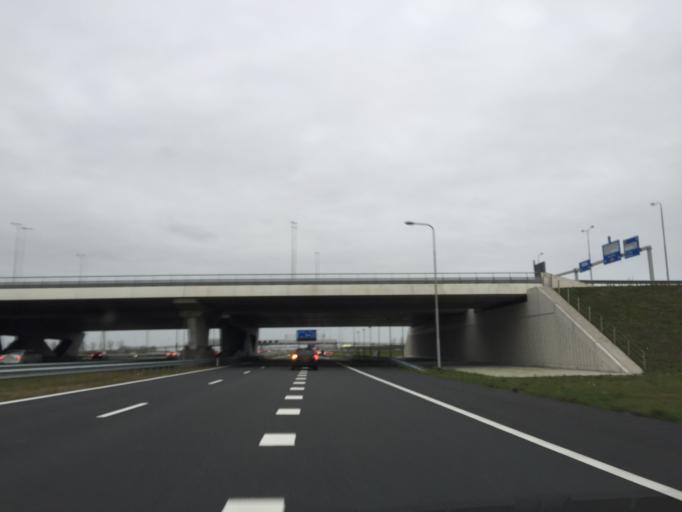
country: NL
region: North Holland
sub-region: Gemeente Haarlemmermeer
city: Hoofddorp
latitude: 52.2841
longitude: 4.7200
